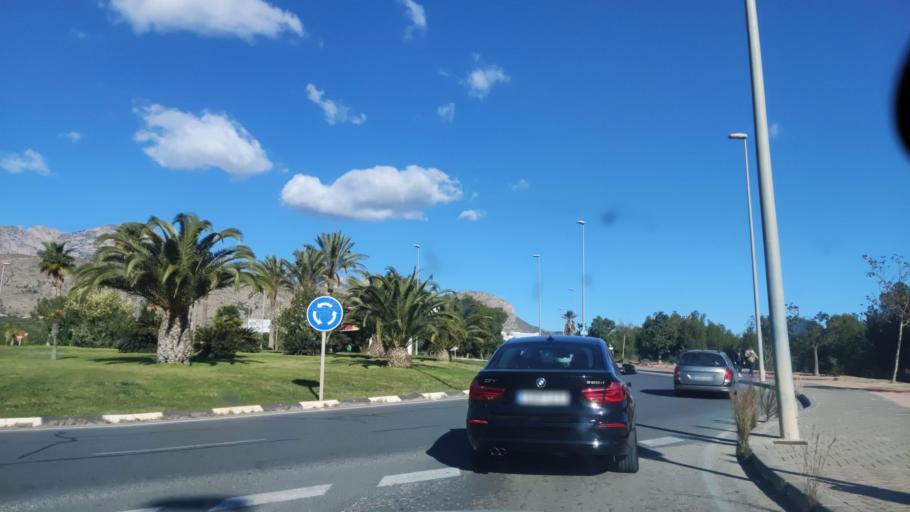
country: ES
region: Valencia
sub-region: Provincia de Alicante
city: Benidorm
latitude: 38.5427
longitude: -0.1600
